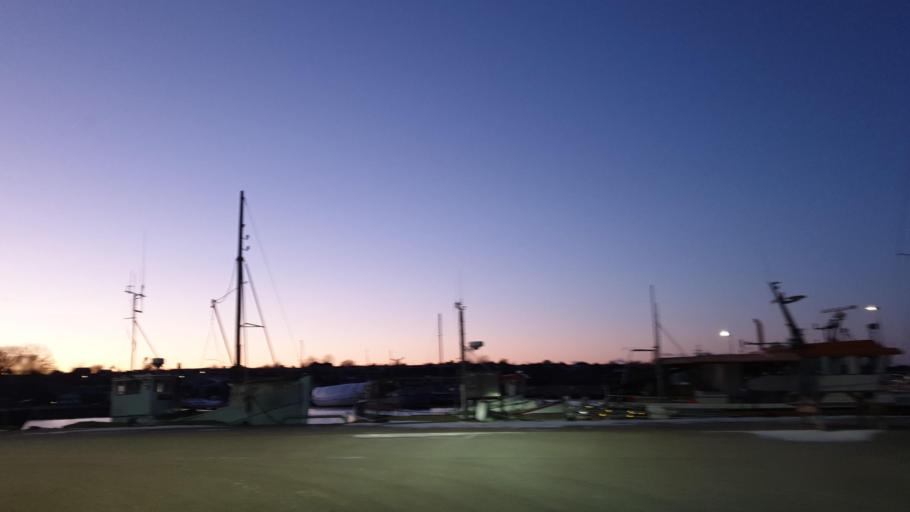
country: SE
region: Gotland
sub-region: Gotland
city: Slite
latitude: 57.4219
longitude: 18.9164
